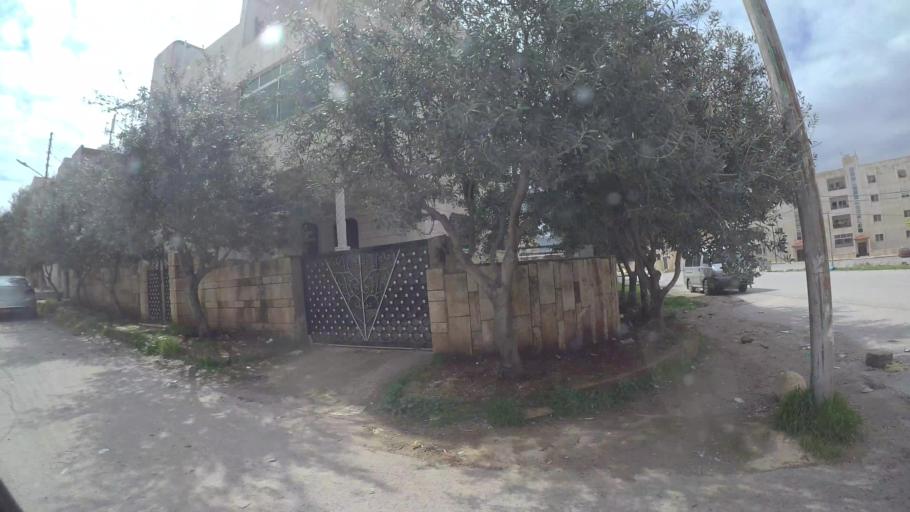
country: JO
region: Amman
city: Al Jubayhah
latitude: 32.0536
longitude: 35.8230
